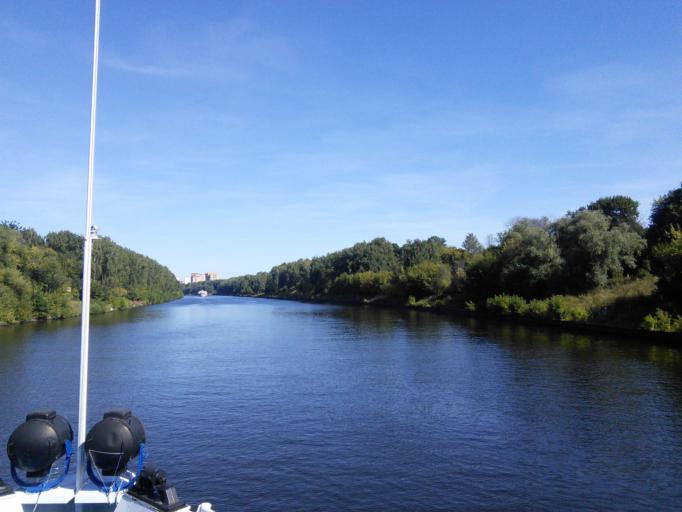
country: RU
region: Moskovskaya
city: Dolgoprudnyy
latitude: 55.9181
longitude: 37.4878
